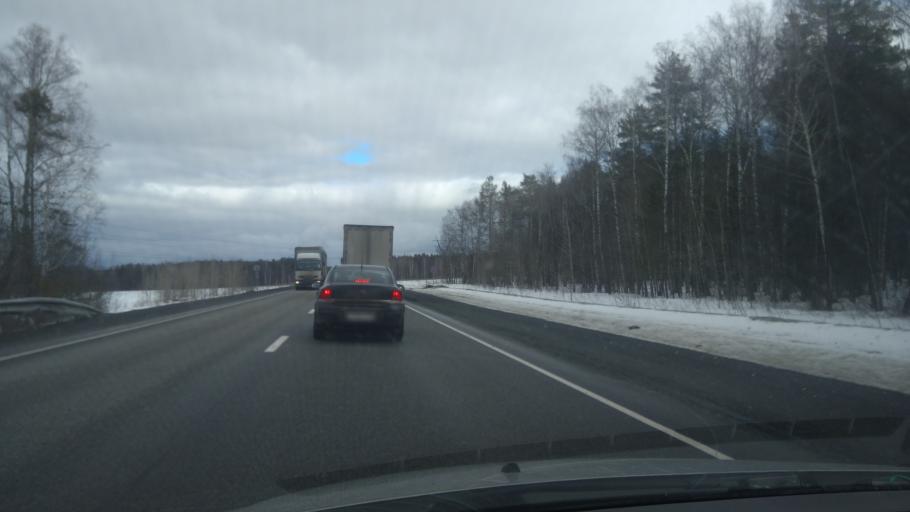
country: RU
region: Sverdlovsk
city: Bisert'
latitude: 56.8224
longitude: 58.7617
